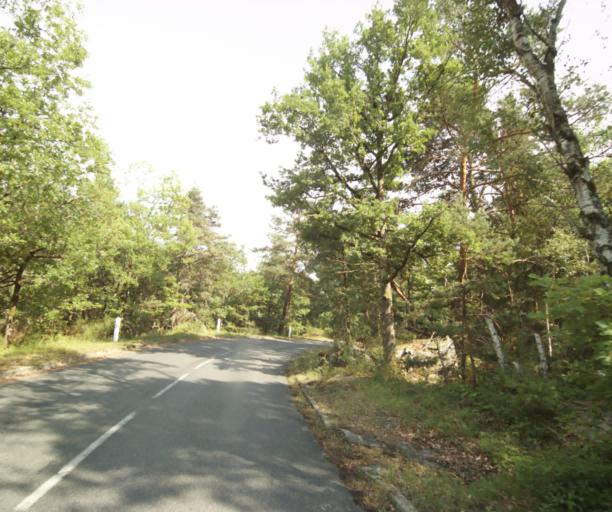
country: FR
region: Ile-de-France
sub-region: Departement de Seine-et-Marne
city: Arbonne-la-Foret
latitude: 48.3849
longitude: 2.5633
